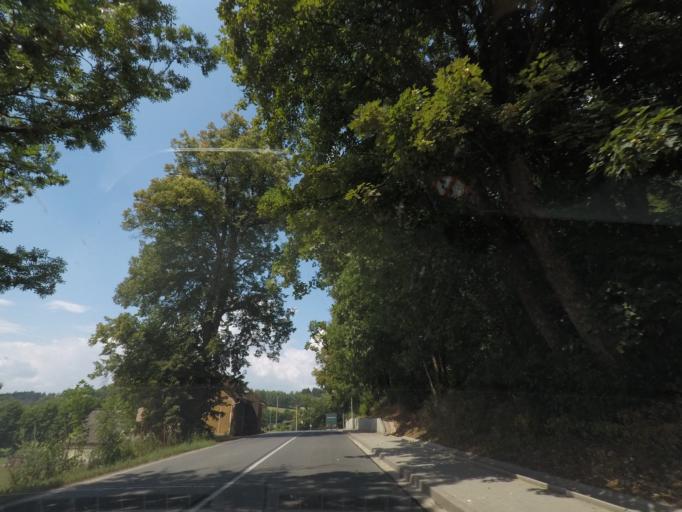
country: CZ
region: Kralovehradecky
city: Pilnikov
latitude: 50.5315
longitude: 15.8127
